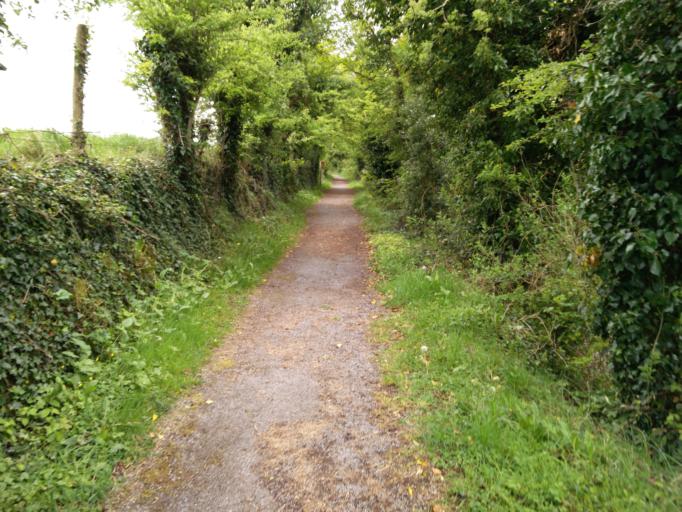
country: IE
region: Connaught
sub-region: Maigh Eo
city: Ballinrobe
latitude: 53.6256
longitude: -9.2404
